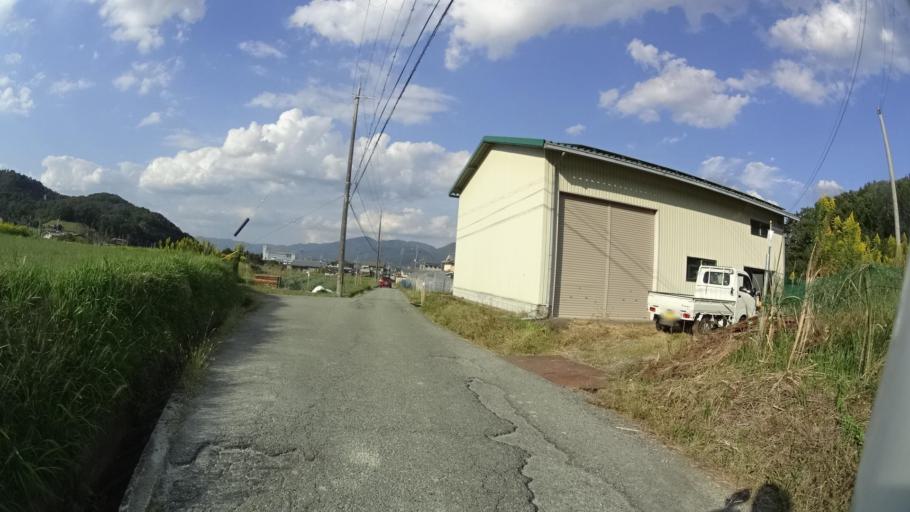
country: JP
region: Kyoto
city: Kameoka
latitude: 35.0042
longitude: 135.5743
